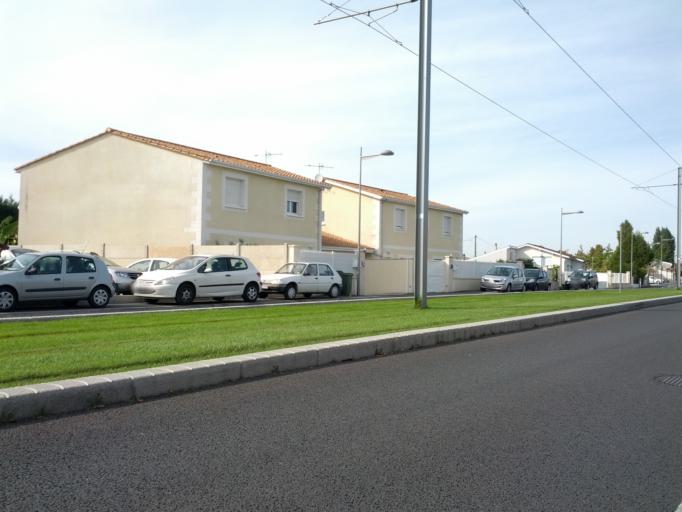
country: FR
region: Aquitaine
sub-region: Departement de la Gironde
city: Begles
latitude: 44.8063
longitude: -0.5513
